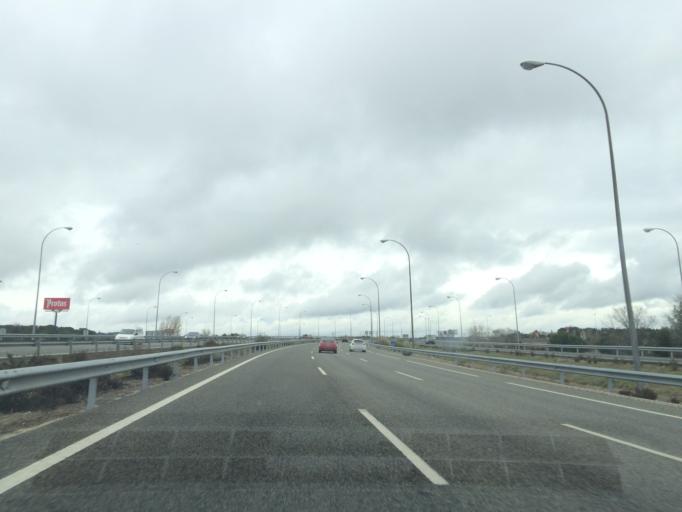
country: ES
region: Madrid
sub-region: Provincia de Madrid
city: Pozuelo de Alarcon
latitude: 40.4282
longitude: -3.8363
